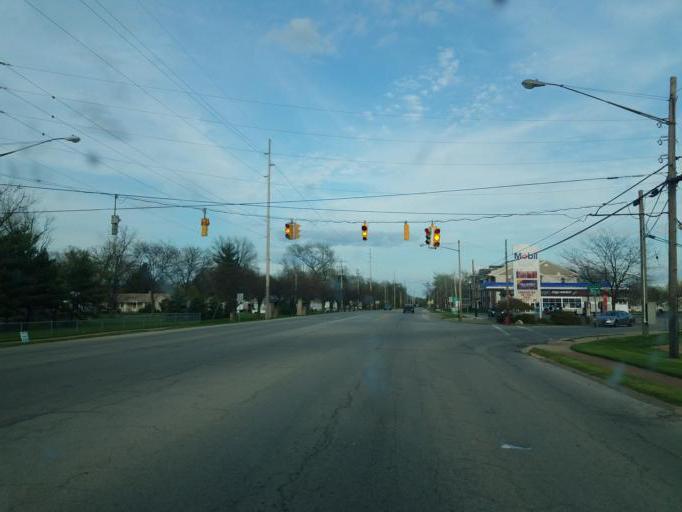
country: US
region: Ohio
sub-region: Erie County
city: Huron
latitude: 41.3890
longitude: -82.5424
